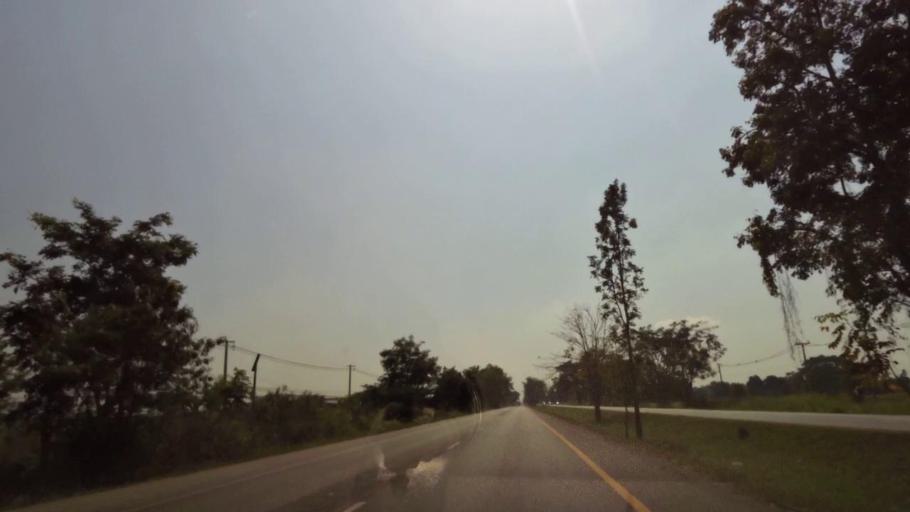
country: TH
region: Phichit
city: Bueng Na Rang
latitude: 16.2844
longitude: 100.1275
